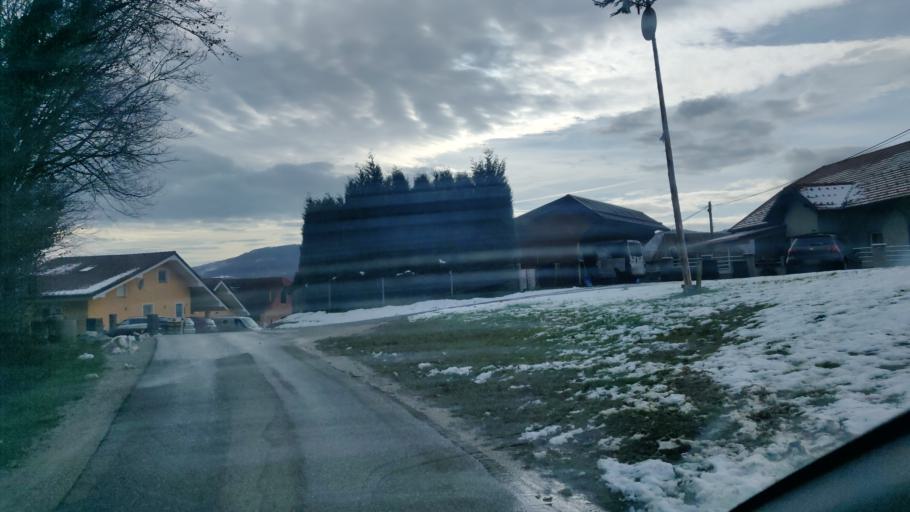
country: SI
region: Makole
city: Makole
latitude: 46.3290
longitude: 15.6558
